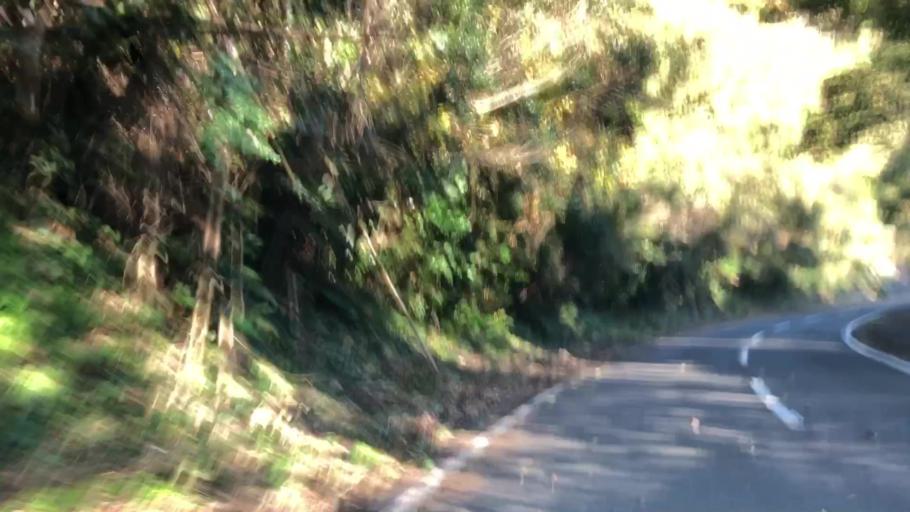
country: JP
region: Nagasaki
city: Sasebo
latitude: 33.0274
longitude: 129.6634
